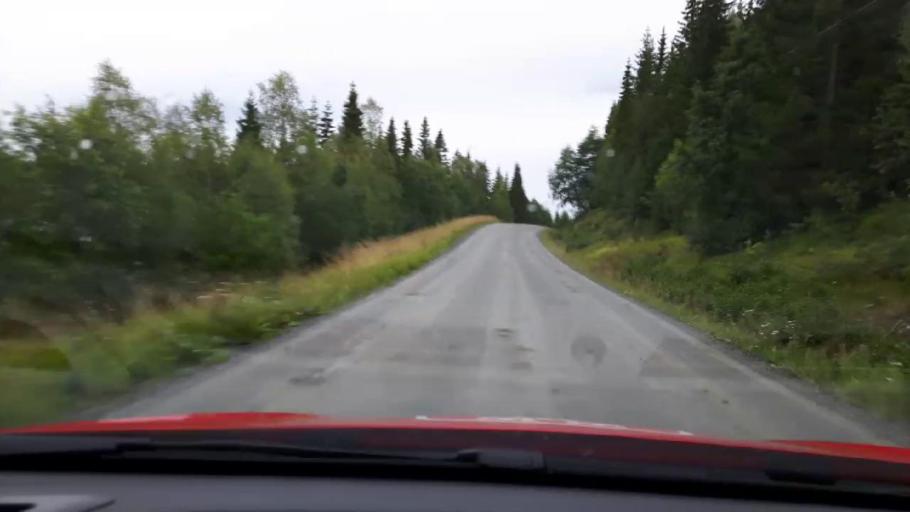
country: SE
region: Jaemtland
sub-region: Are Kommun
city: Jarpen
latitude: 63.4157
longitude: 13.3542
